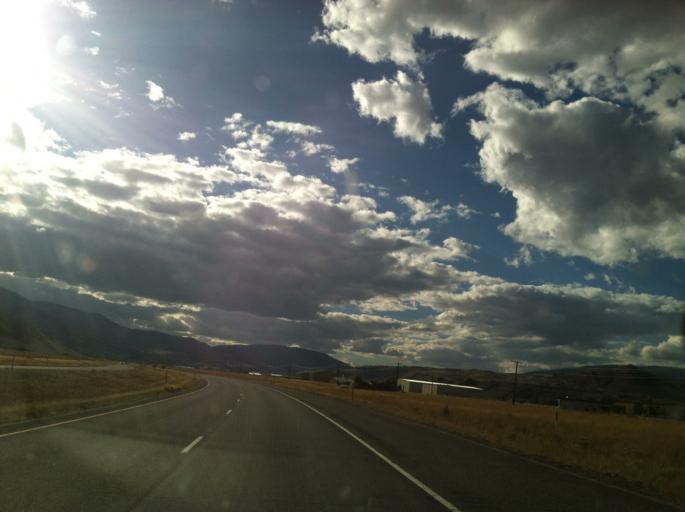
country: US
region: Montana
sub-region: Deer Lodge County
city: Anaconda
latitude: 46.1282
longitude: -112.8998
